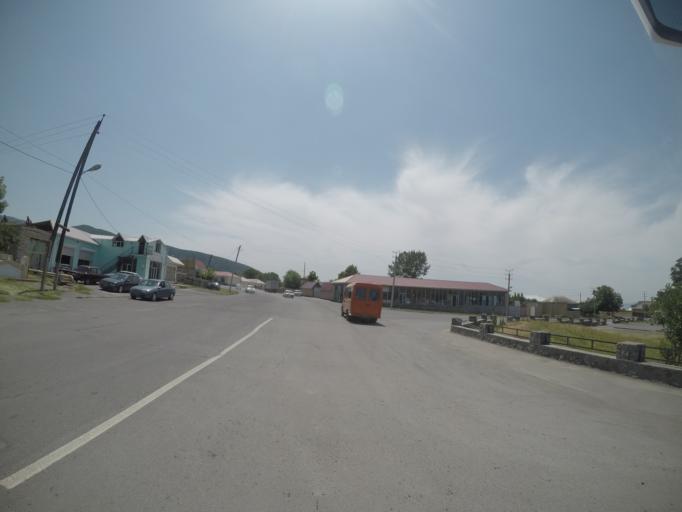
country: AZ
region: Qakh Rayon
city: Qax
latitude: 41.4159
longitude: 46.9068
